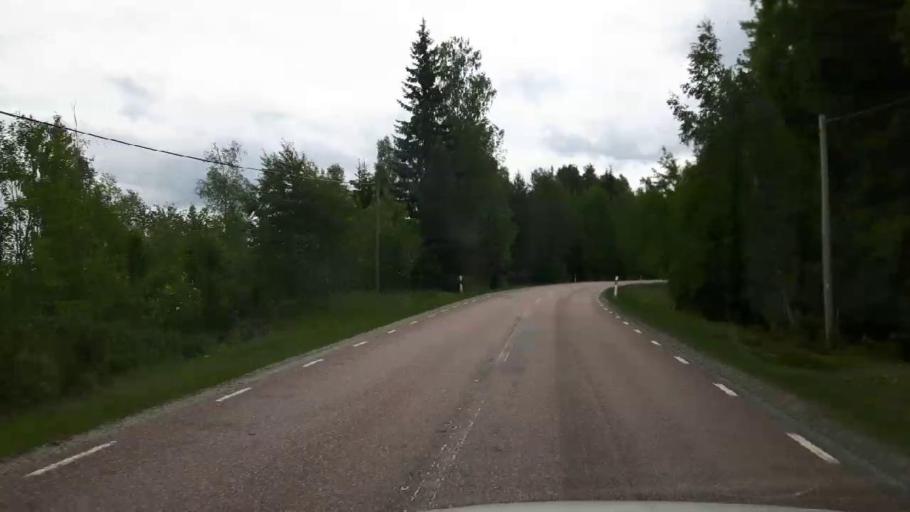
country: SE
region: Vaestmanland
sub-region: Fagersta Kommun
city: Fagersta
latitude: 59.9310
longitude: 15.8271
